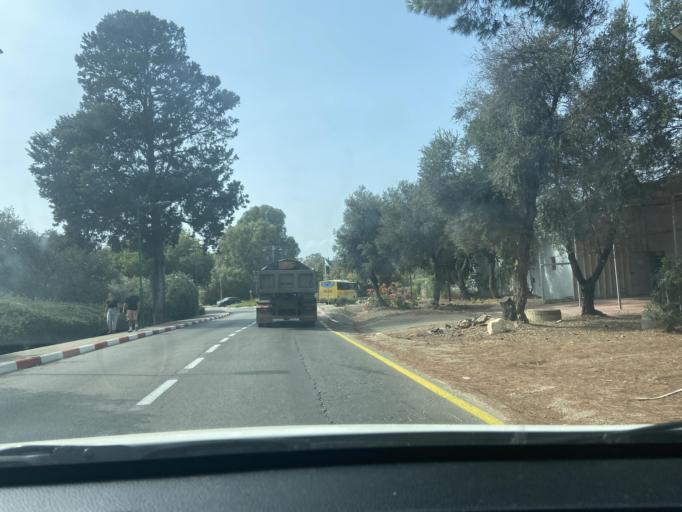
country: IL
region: Northern District
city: Nahariya
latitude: 33.0444
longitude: 35.1096
